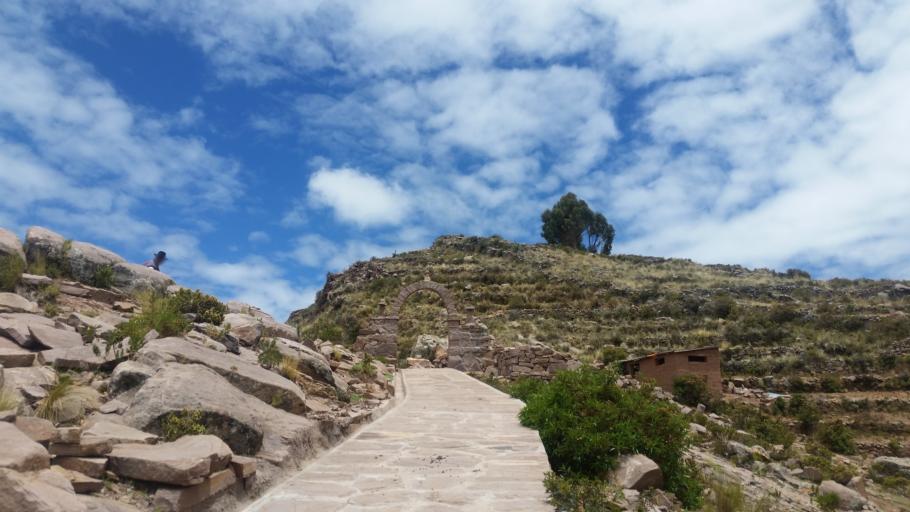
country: PE
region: Puno
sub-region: Provincia de Puno
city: Taquile
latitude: -15.7917
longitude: -69.6818
